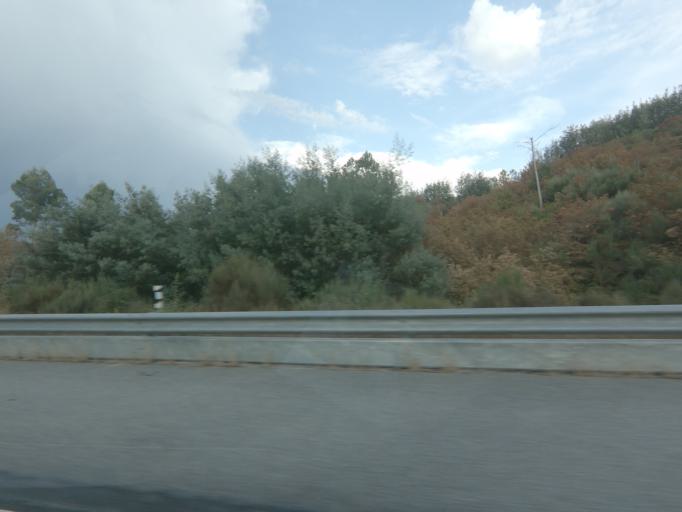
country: PT
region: Viseu
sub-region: Castro Daire
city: Castro Daire
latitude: 40.8815
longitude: -7.9197
